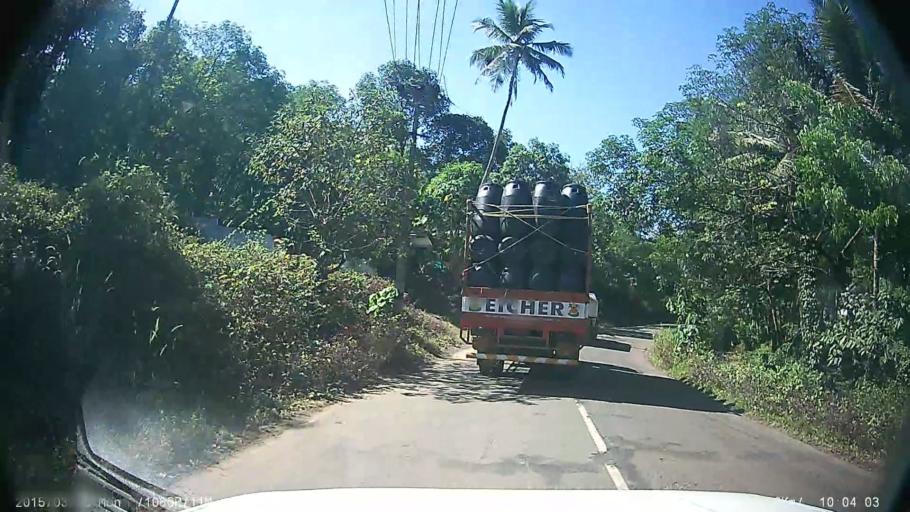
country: IN
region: Kerala
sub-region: Kottayam
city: Palackattumala
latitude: 9.7765
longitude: 76.5732
